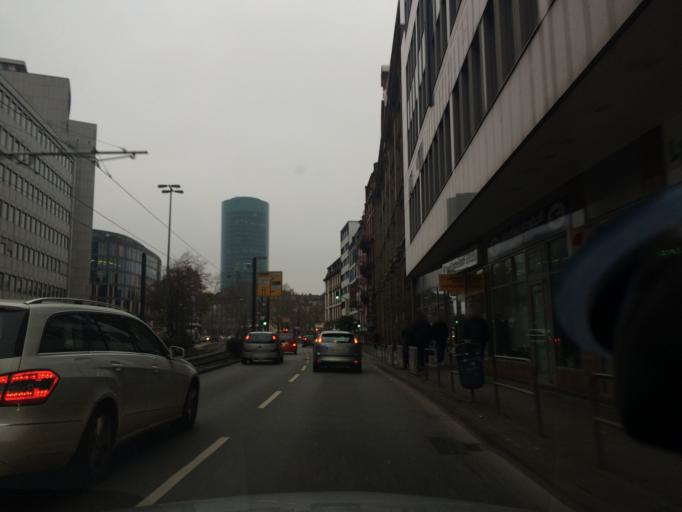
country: DE
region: Hesse
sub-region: Regierungsbezirk Darmstadt
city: Frankfurt am Main
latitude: 50.1054
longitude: 8.6648
